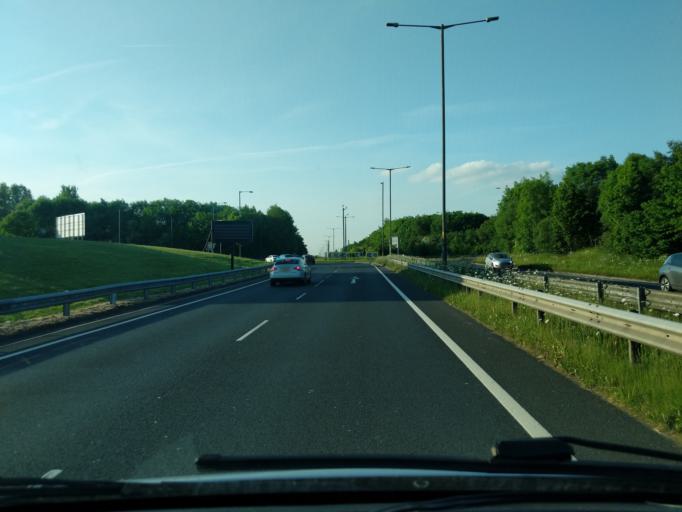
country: GB
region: England
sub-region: St. Helens
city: St Helens
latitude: 53.4274
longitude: -2.7401
